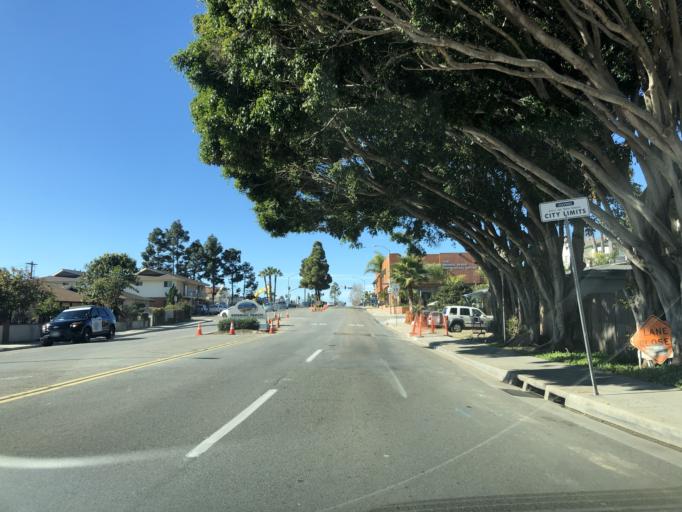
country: US
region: California
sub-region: San Diego County
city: Imperial Beach
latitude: 32.5766
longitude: -117.1037
